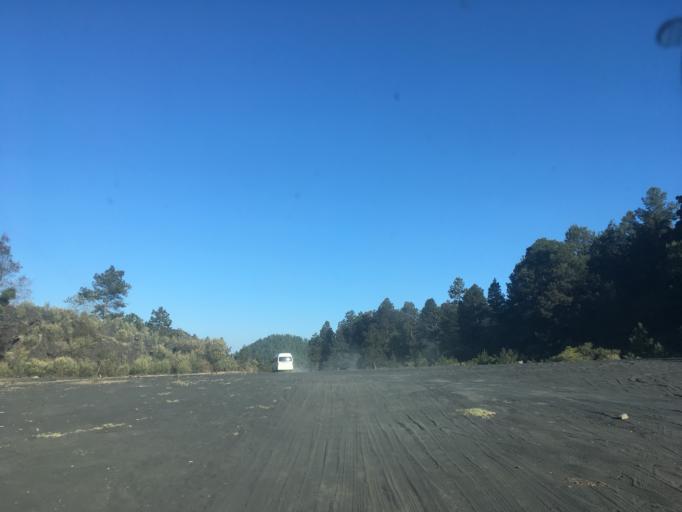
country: MX
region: Michoacan
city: Angahuan
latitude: 19.4823
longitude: -102.2529
